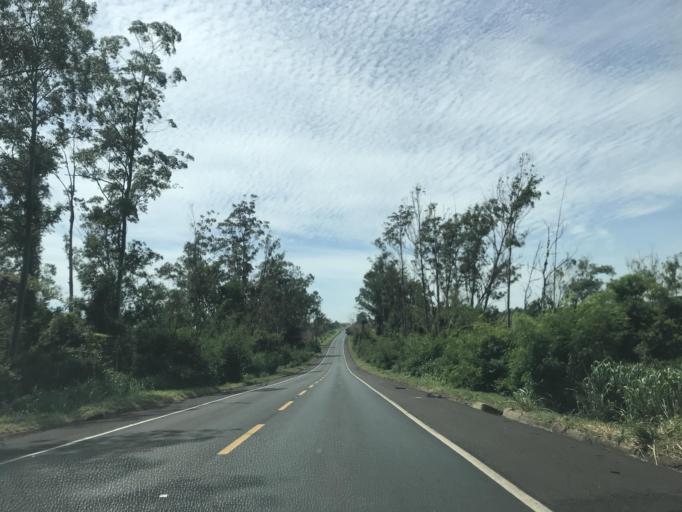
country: BR
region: Parana
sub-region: Paranavai
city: Paranavai
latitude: -22.9986
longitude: -52.5711
